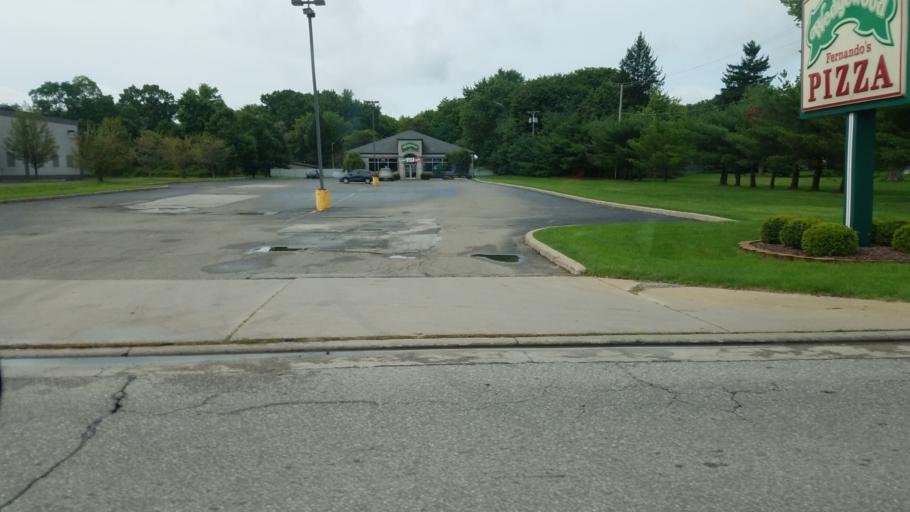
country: US
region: Ohio
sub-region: Mahoning County
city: Poland
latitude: 41.0361
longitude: -80.6348
